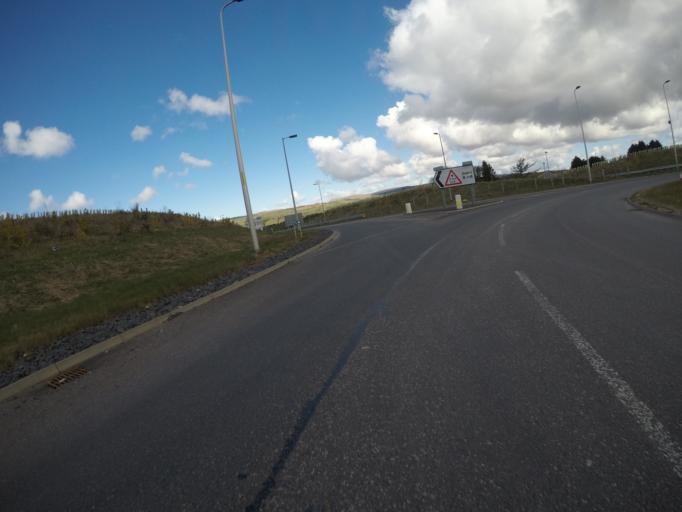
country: GB
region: Scotland
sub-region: North Ayrshire
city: Dalry
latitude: 55.7135
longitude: -4.6944
